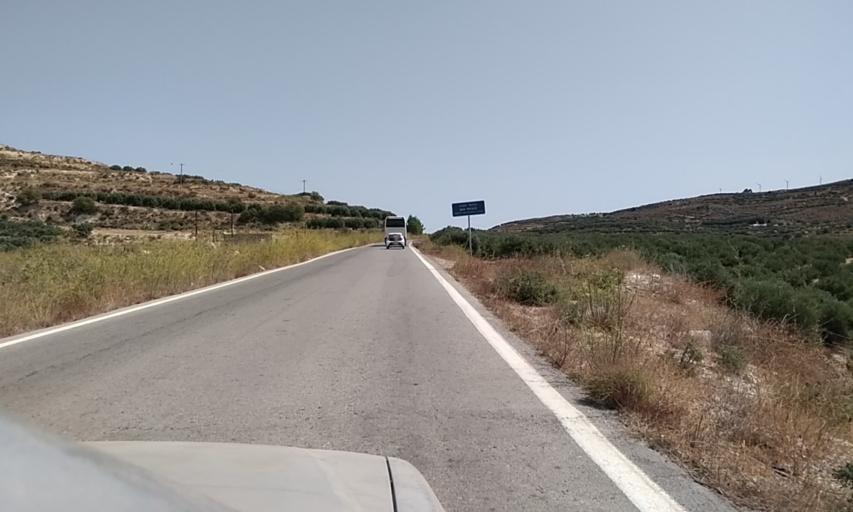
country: GR
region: Crete
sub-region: Nomos Lasithiou
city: Makry-Gialos
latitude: 35.0984
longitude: 26.0611
